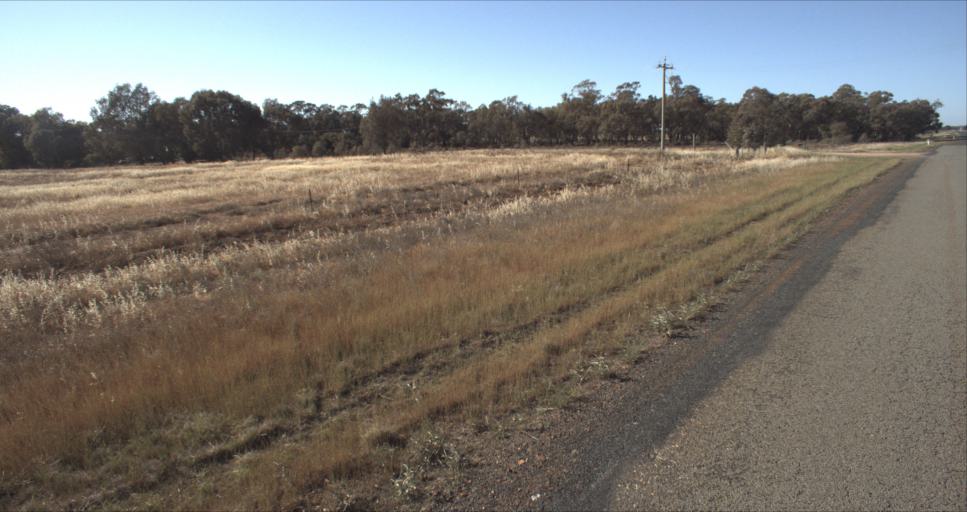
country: AU
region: New South Wales
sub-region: Leeton
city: Leeton
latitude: -34.5614
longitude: 146.2653
